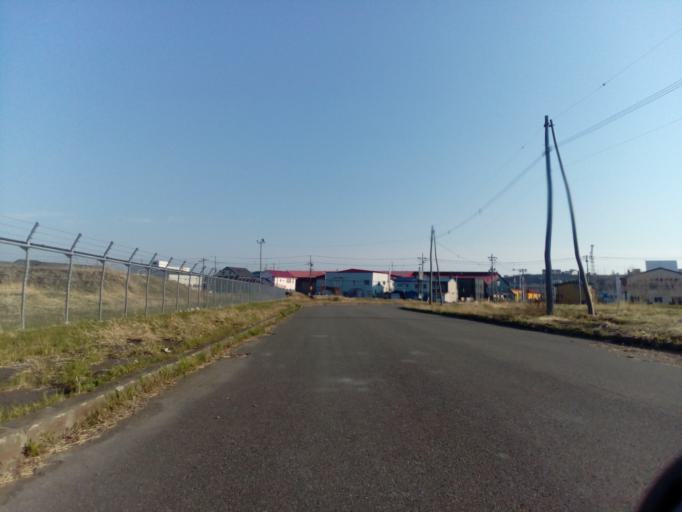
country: JP
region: Hokkaido
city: Wakkanai
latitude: 45.4038
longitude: 141.6878
